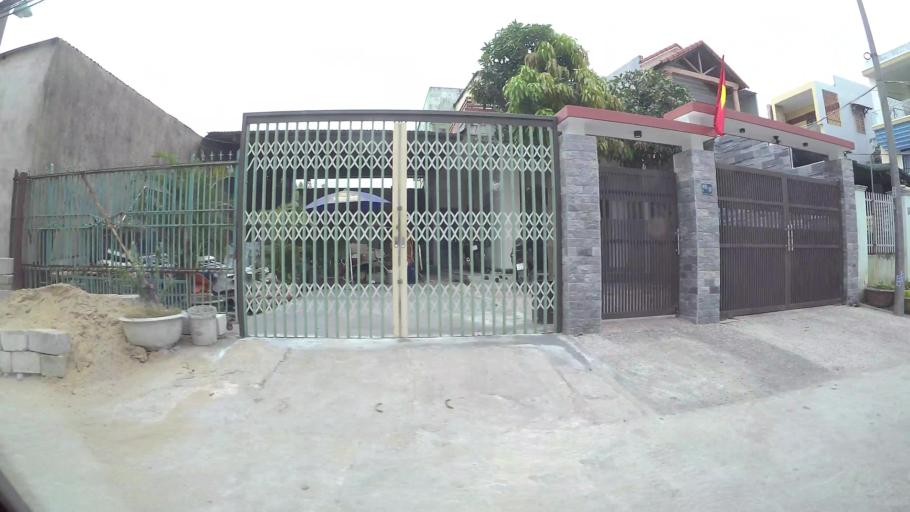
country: VN
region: Da Nang
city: Thanh Khe
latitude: 16.0647
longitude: 108.1910
